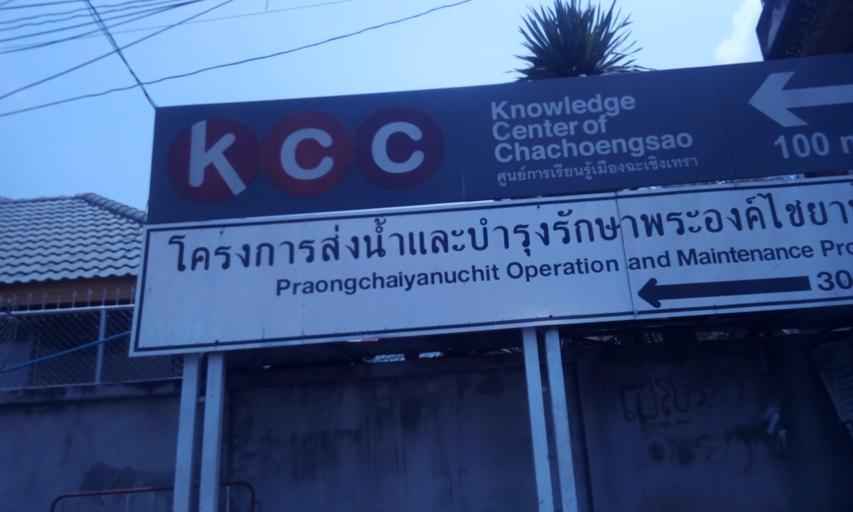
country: TH
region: Chachoengsao
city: Chachoengsao
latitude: 13.6916
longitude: 101.0751
